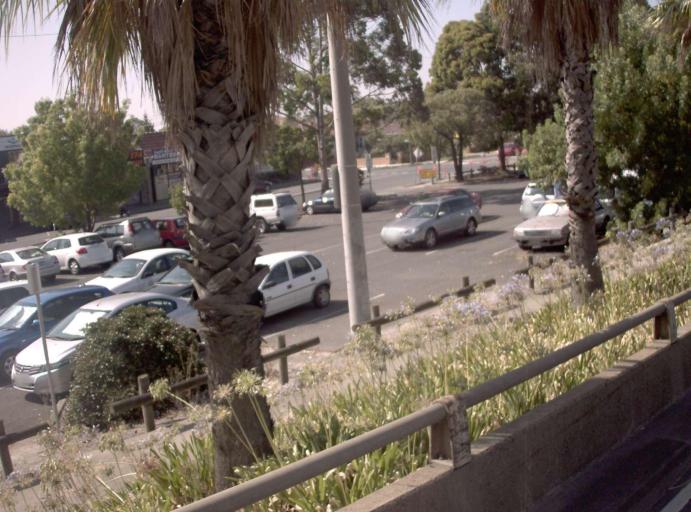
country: AU
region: Victoria
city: Hughesdale
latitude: -37.9004
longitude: 145.0871
